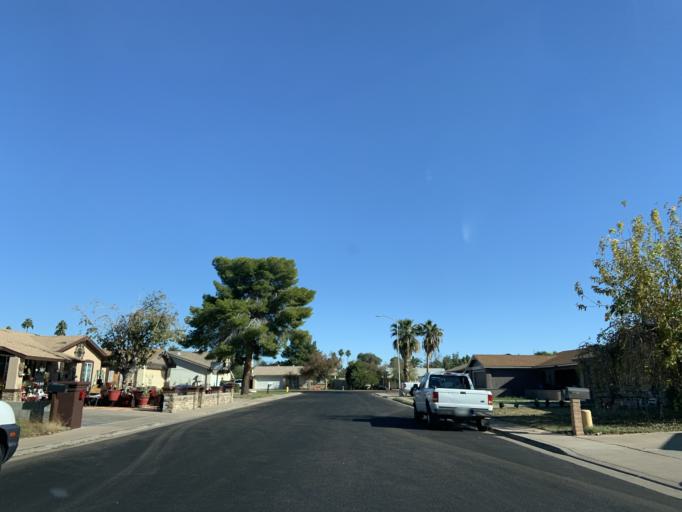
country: US
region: Arizona
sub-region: Maricopa County
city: San Carlos
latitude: 33.3589
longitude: -111.8692
